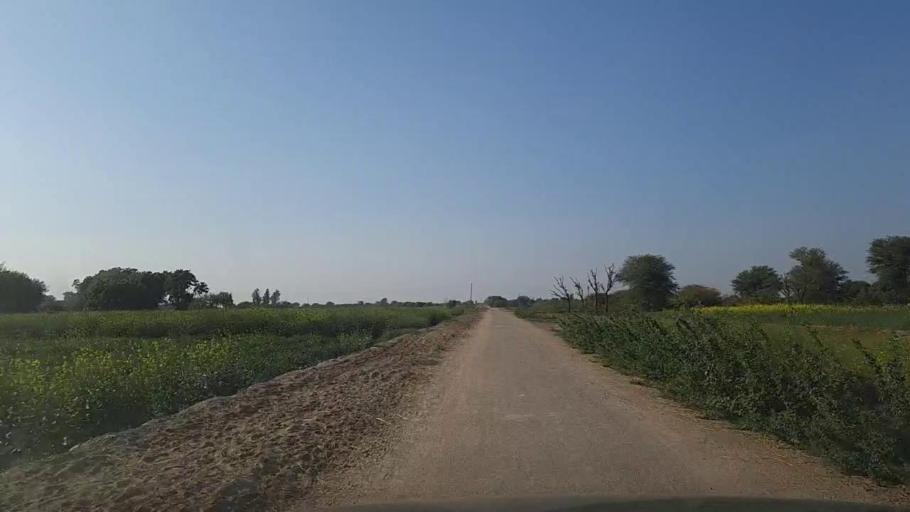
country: PK
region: Sindh
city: Digri
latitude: 25.0209
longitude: 69.2312
